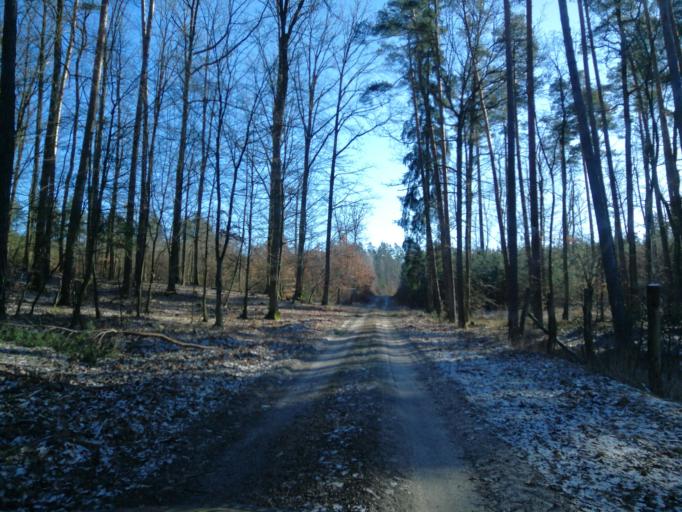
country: PL
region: Kujawsko-Pomorskie
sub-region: Powiat brodnicki
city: Gorzno
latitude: 53.2188
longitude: 19.7099
